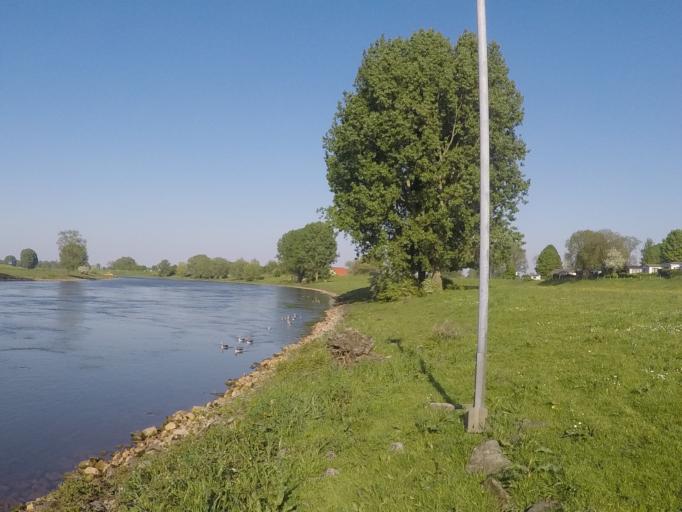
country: NL
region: Gelderland
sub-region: Gemeente Rheden
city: Rheden
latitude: 51.9955
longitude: 6.0267
